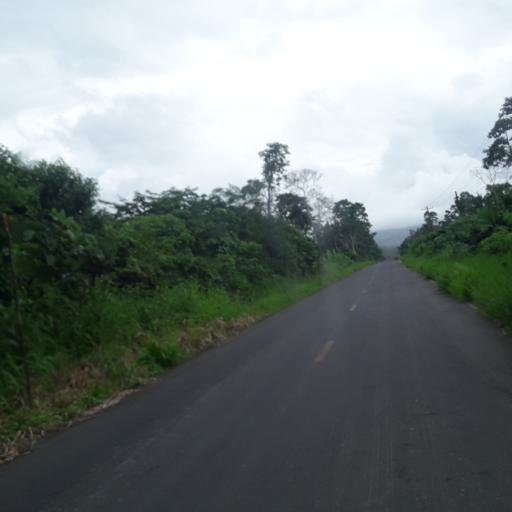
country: EC
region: Napo
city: Tena
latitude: -1.0482
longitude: -77.6637
